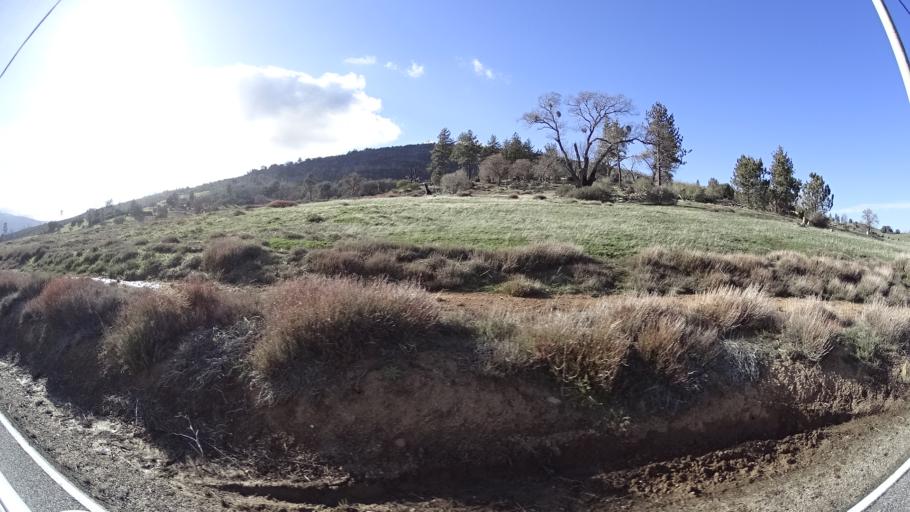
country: US
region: California
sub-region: San Diego County
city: Julian
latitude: 32.9979
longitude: -116.5679
